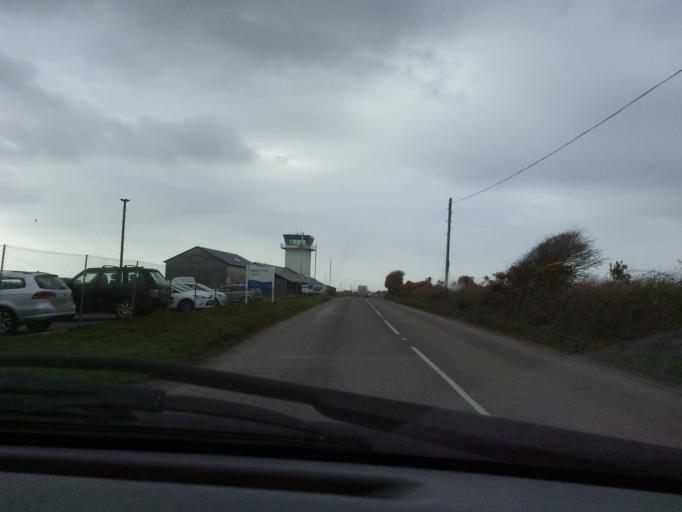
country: GB
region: England
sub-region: Cornwall
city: Saint Just
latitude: 50.1015
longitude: -5.6667
